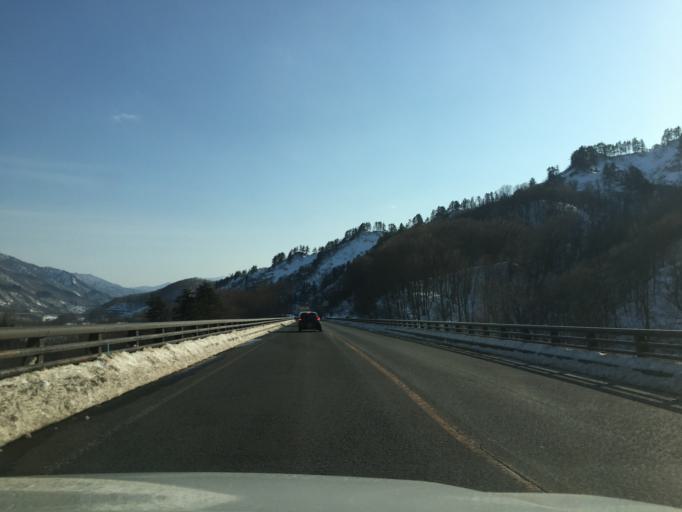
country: JP
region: Yamagata
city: Sagae
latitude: 38.4641
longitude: 139.9919
